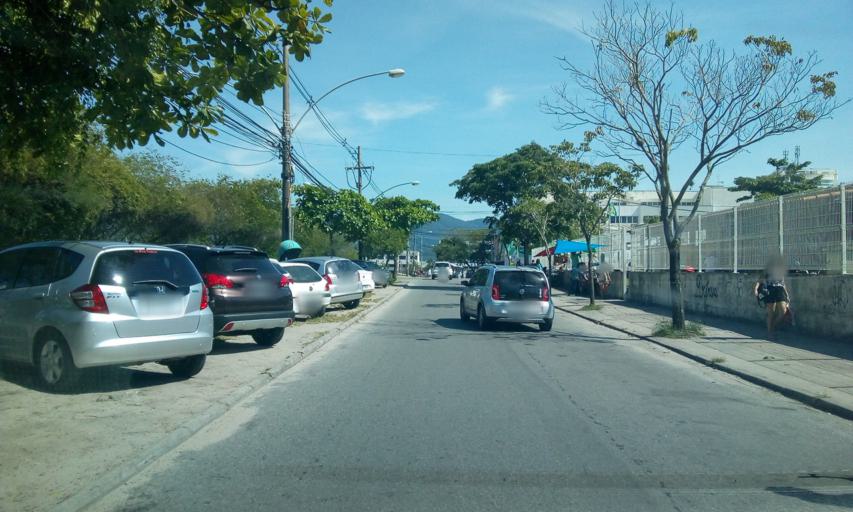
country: BR
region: Rio de Janeiro
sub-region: Nilopolis
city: Nilopolis
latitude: -23.0206
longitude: -43.4828
